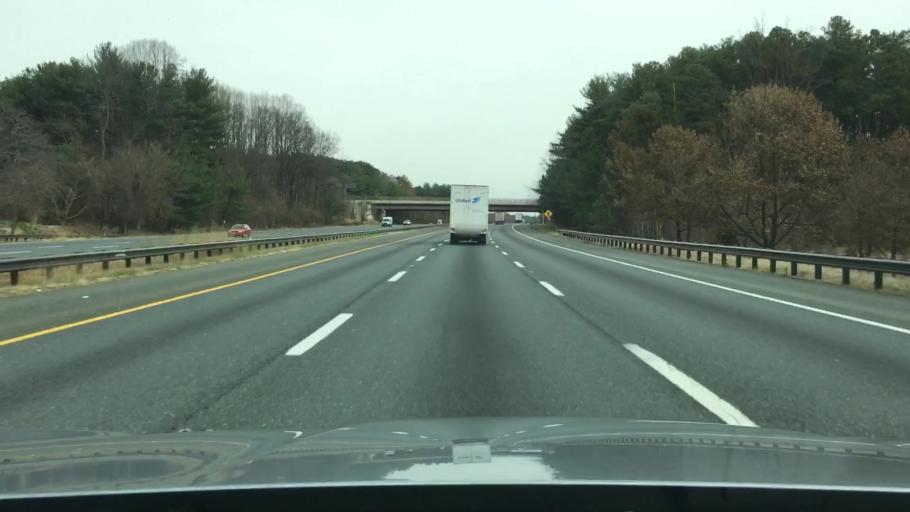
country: US
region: Maryland
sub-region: Anne Arundel County
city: Davidsonville
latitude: 38.9599
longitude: -76.6595
